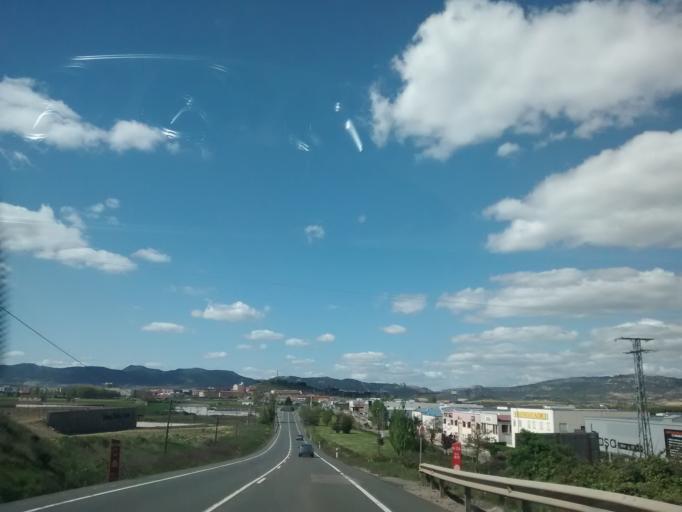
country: ES
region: La Rioja
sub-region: Provincia de La Rioja
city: Ollauri
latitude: 42.5567
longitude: -2.8358
